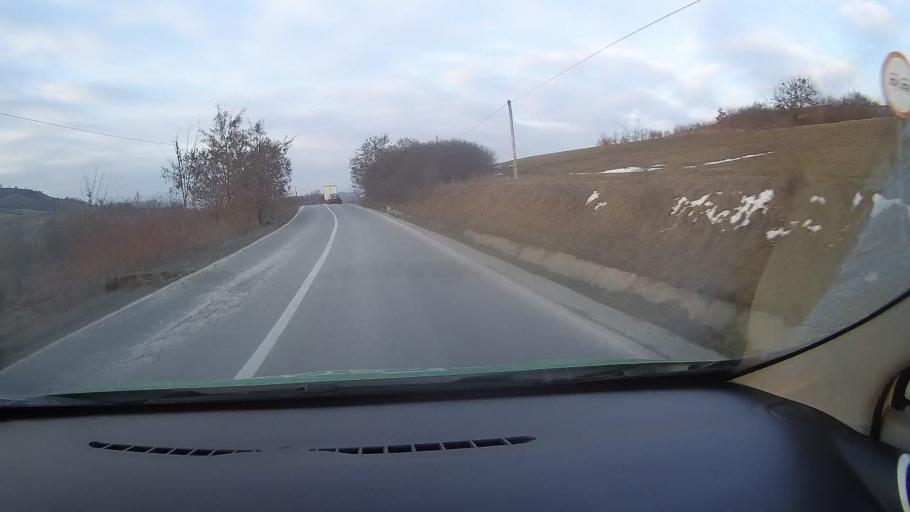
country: RO
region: Harghita
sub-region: Comuna Simonesti
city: Simonesti
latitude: 46.3251
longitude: 25.1018
